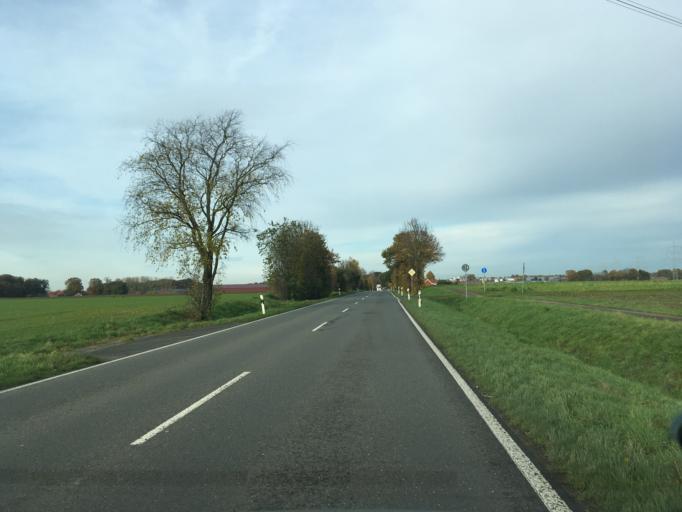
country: DE
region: North Rhine-Westphalia
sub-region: Regierungsbezirk Munster
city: Heiden
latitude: 51.8061
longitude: 6.9508
